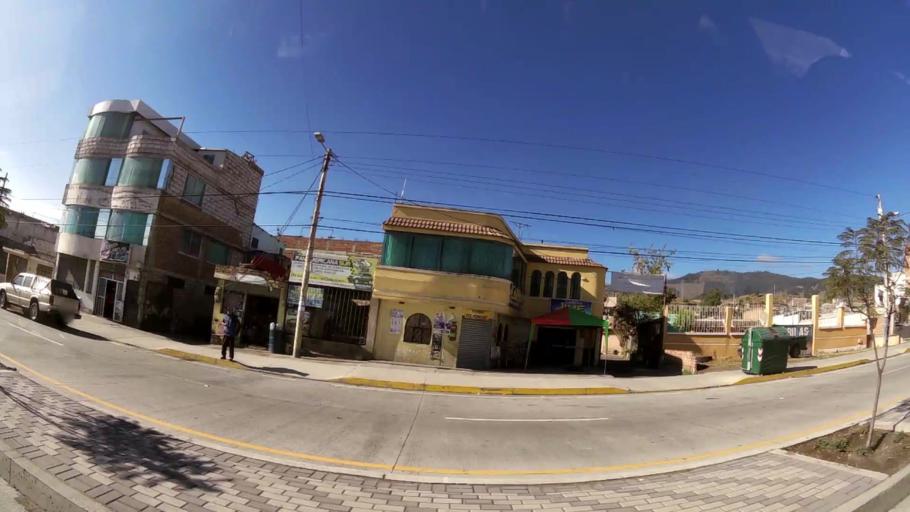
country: EC
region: Chimborazo
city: Riobamba
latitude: -1.6568
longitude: -78.6925
